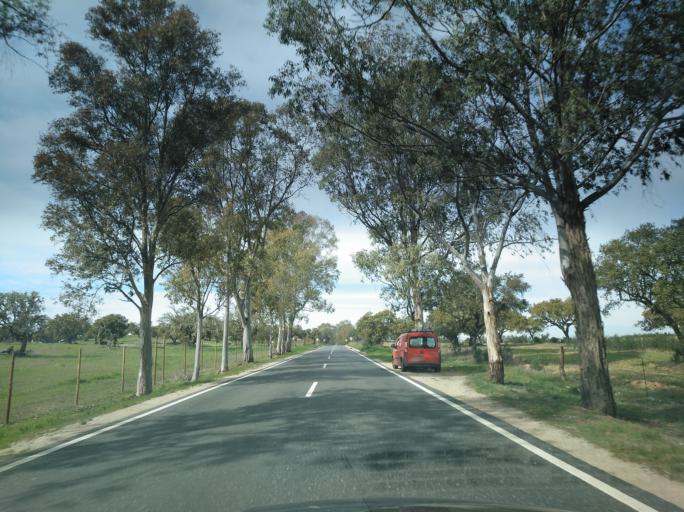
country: PT
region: Beja
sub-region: Mertola
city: Mertola
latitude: 37.7311
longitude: -7.7684
